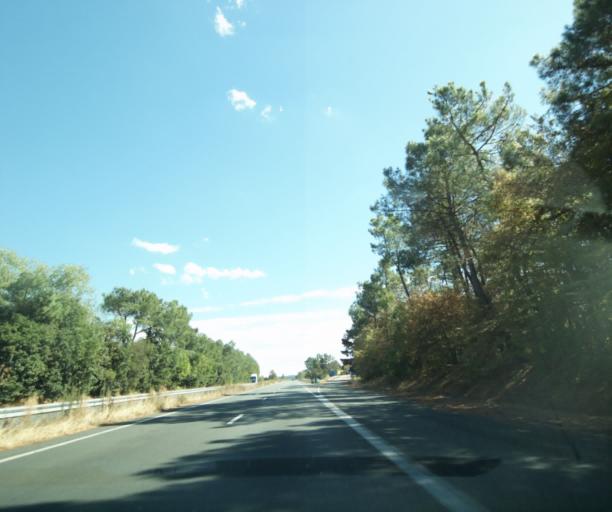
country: FR
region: Aquitaine
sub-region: Departement du Lot-et-Garonne
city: Buzet-sur-Baise
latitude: 44.2514
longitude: 0.2984
